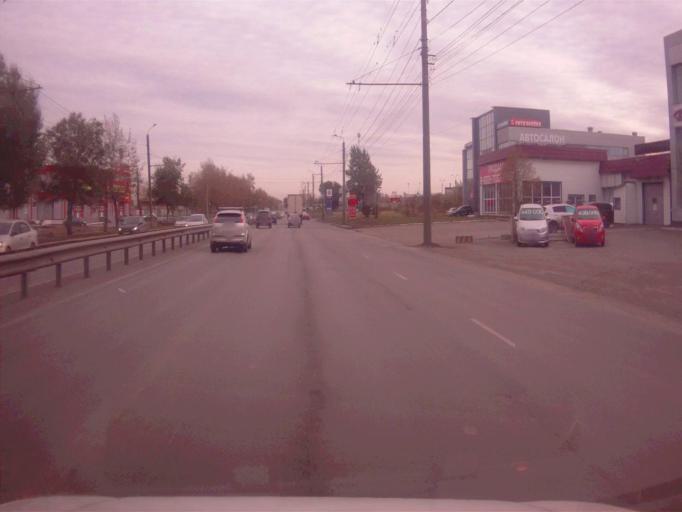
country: RU
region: Chelyabinsk
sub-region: Gorod Chelyabinsk
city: Chelyabinsk
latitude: 55.1391
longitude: 61.4569
